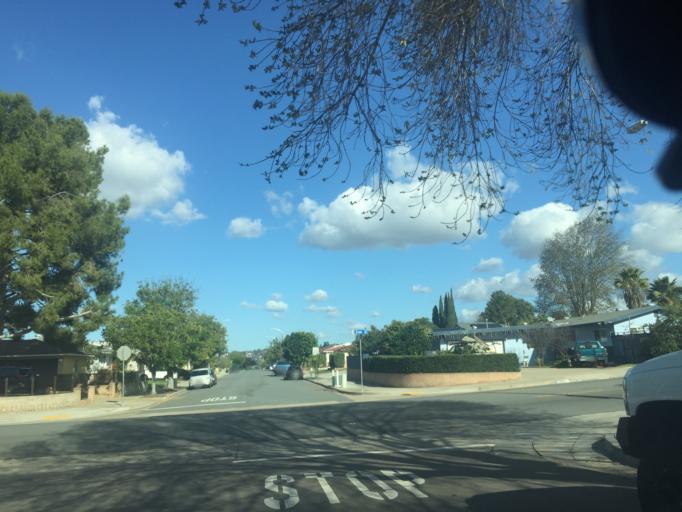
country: US
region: California
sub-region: San Diego County
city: La Mesa
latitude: 32.7927
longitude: -117.0889
